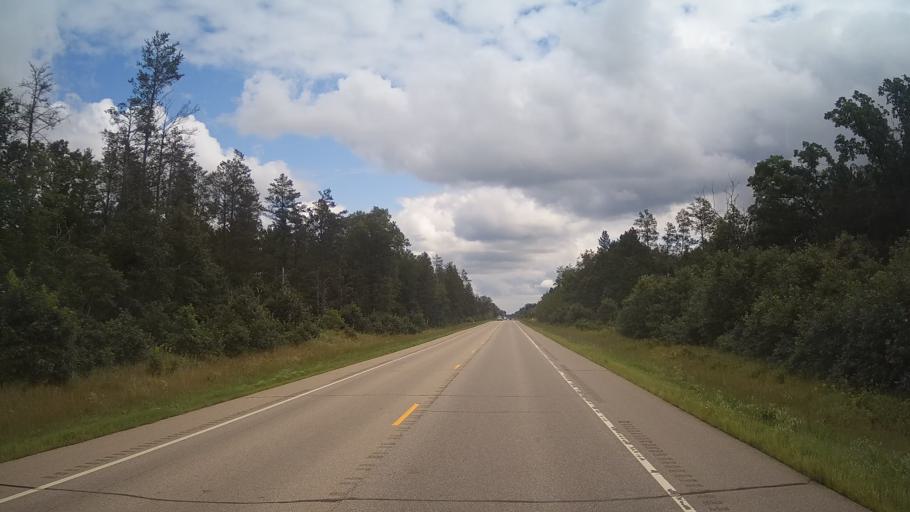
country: US
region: Wisconsin
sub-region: Adams County
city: Friendship
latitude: 44.0252
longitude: -89.7446
